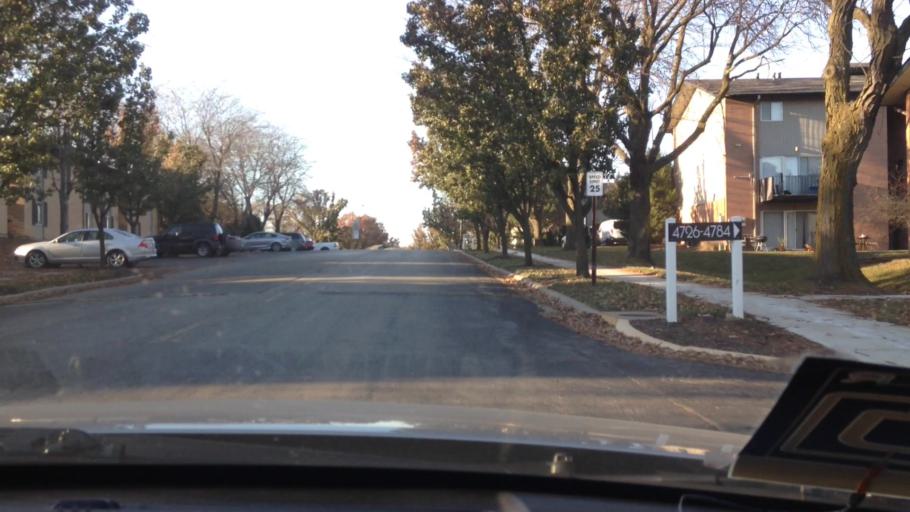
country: US
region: Kansas
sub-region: Johnson County
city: Roeland Park
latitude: 39.0410
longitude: -94.6428
